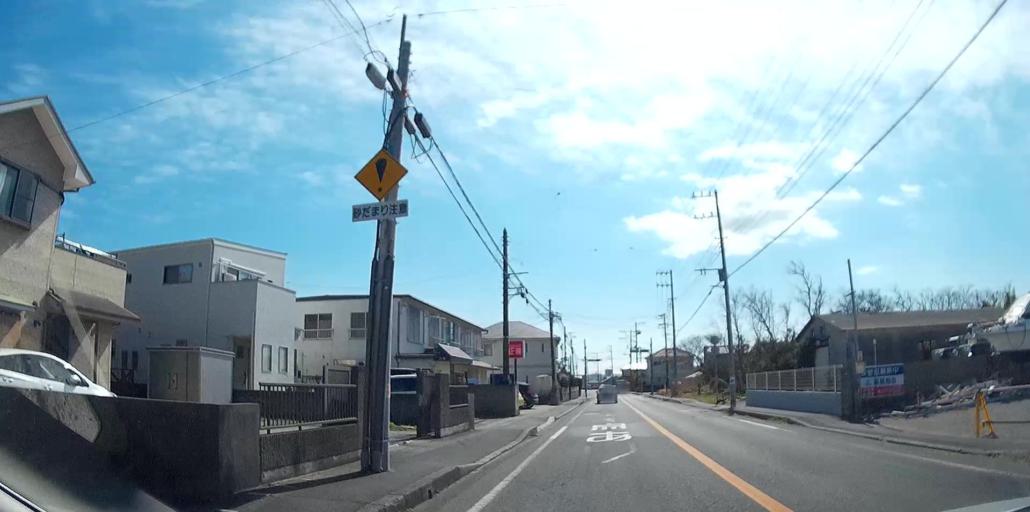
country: JP
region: Chiba
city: Tateyama
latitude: 35.0231
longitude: 139.8548
